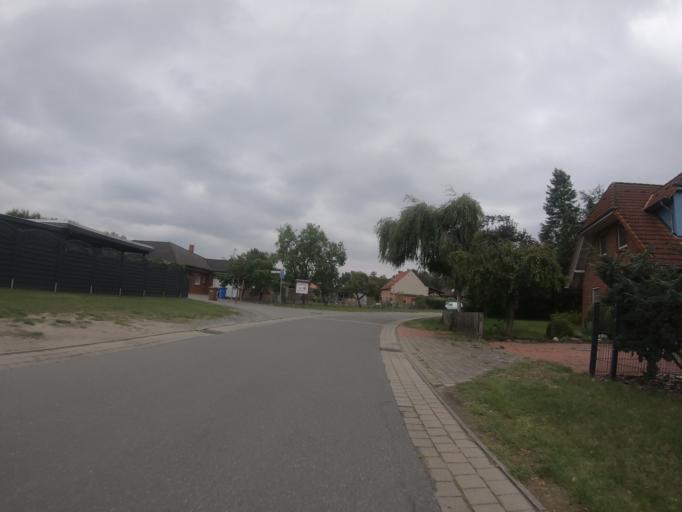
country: DE
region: Lower Saxony
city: Ribbesbuttel
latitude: 52.4338
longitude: 10.5064
